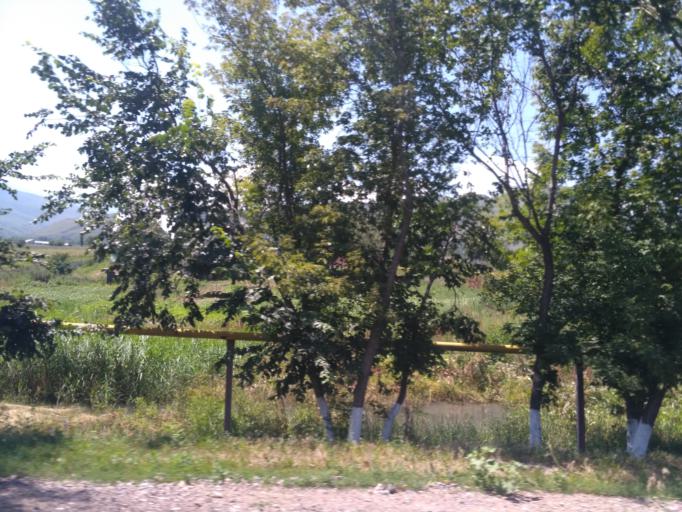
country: KZ
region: Almaty Oblysy
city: Burunday
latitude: 43.1663
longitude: 76.5981
